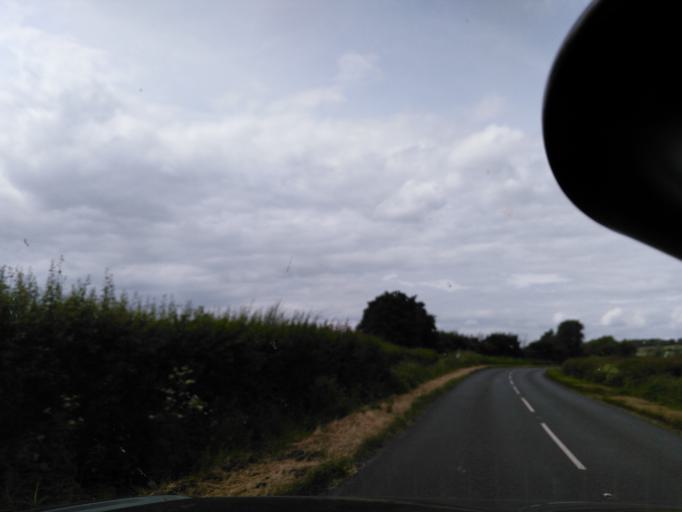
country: GB
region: England
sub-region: Wiltshire
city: Bulkington
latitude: 51.3326
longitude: -2.0776
